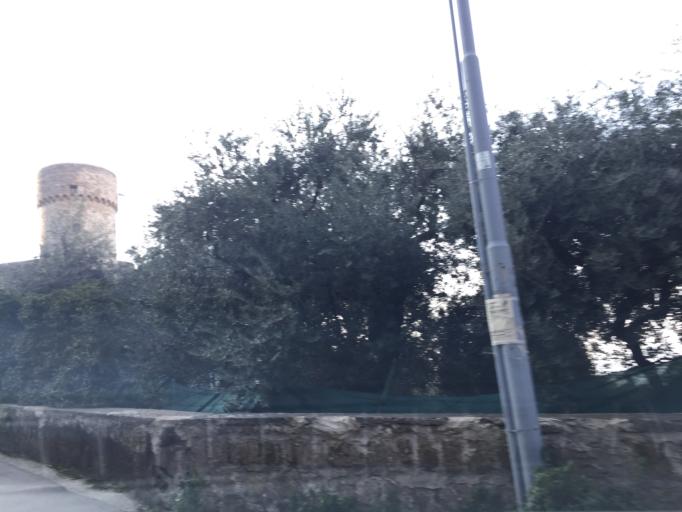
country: IT
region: Campania
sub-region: Provincia di Napoli
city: Castellammare di Stabia
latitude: 40.6883
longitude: 14.4752
